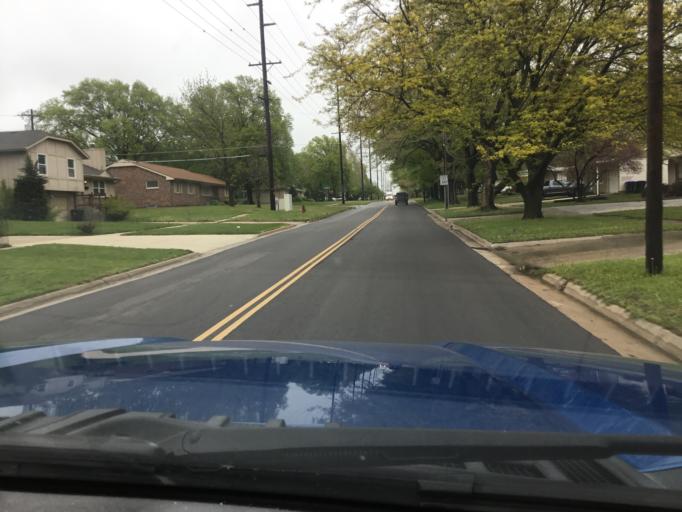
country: US
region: Kansas
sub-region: Shawnee County
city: Topeka
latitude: 39.0364
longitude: -95.7531
